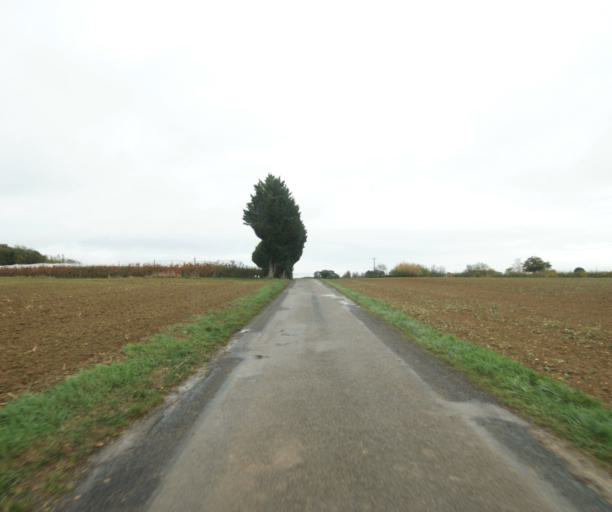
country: FR
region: Bourgogne
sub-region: Departement de Saone-et-Loire
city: Saint-Martin-Belle-Roche
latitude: 46.4792
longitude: 4.8558
